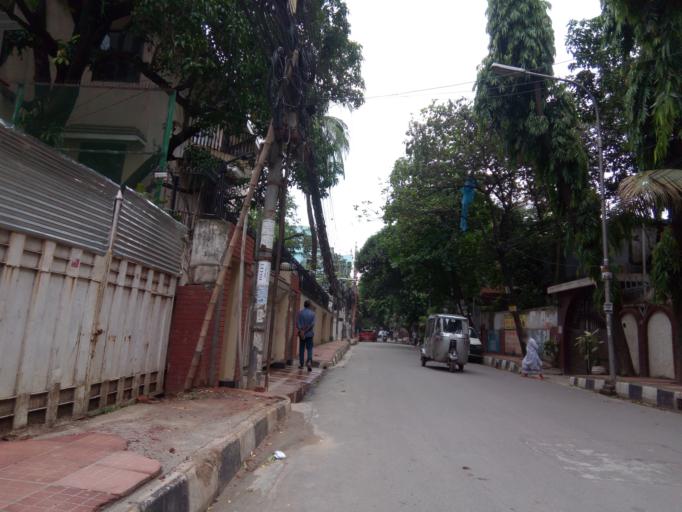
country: BD
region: Dhaka
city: Paltan
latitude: 23.7896
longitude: 90.4010
